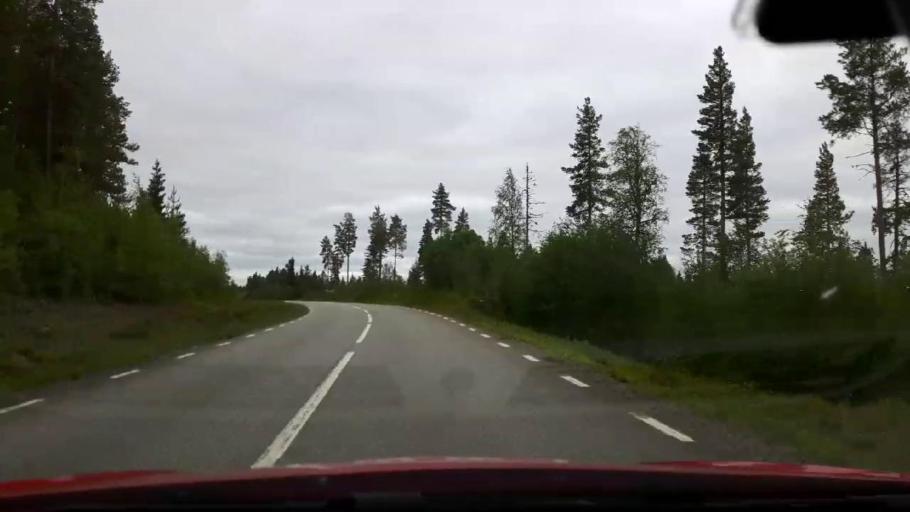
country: SE
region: Jaemtland
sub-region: Stroemsunds Kommun
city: Stroemsund
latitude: 63.3808
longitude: 15.6862
